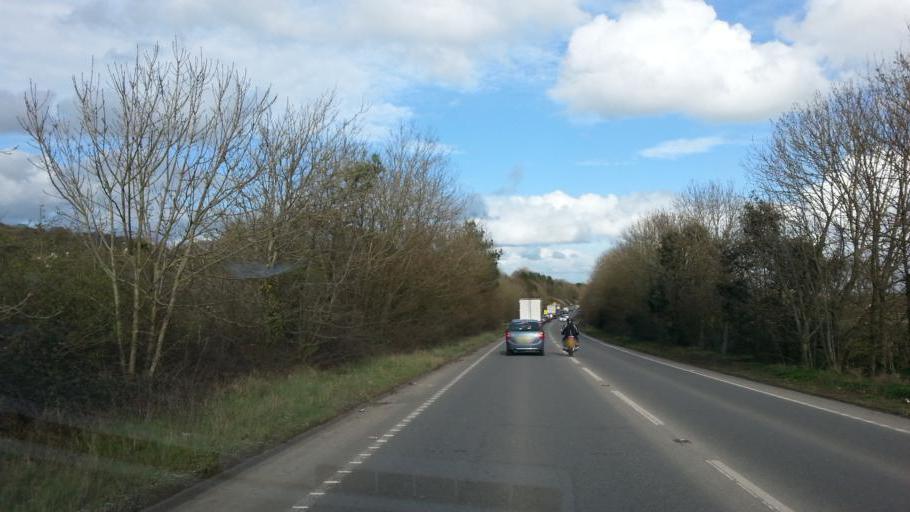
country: GB
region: England
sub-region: Devon
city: Northam
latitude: 51.0293
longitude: -4.2230
